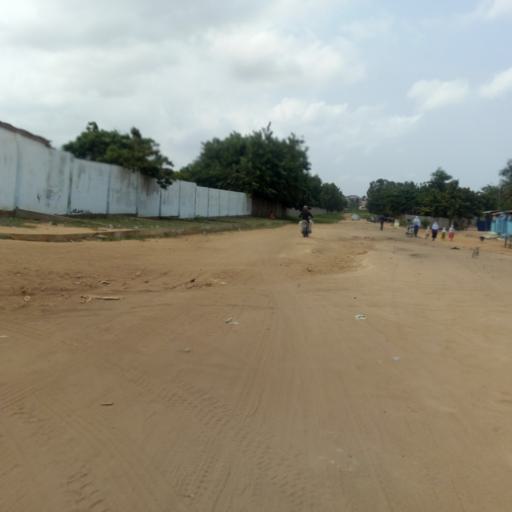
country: TG
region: Maritime
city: Lome
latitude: 6.1871
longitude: 1.1716
